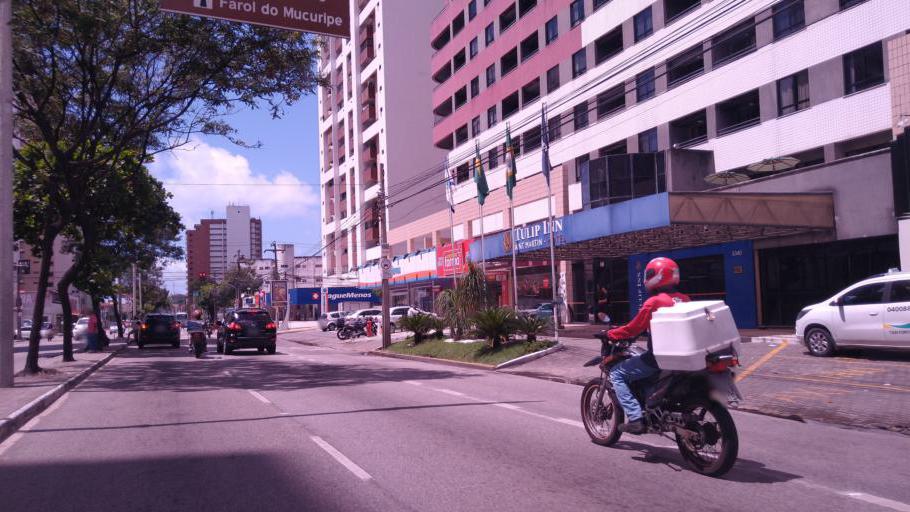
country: BR
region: Ceara
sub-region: Fortaleza
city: Fortaleza
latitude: -3.7265
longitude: -38.4900
